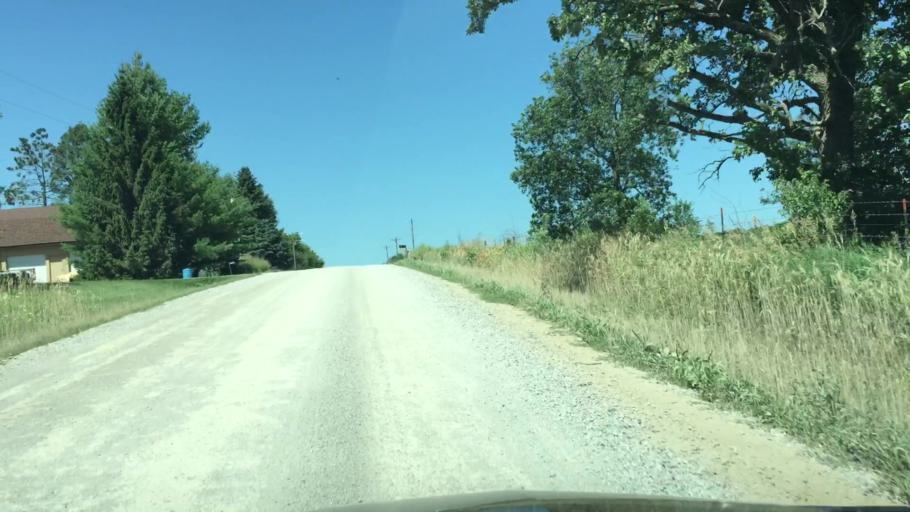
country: US
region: Iowa
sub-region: Linn County
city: Ely
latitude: 41.8329
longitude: -91.5773
